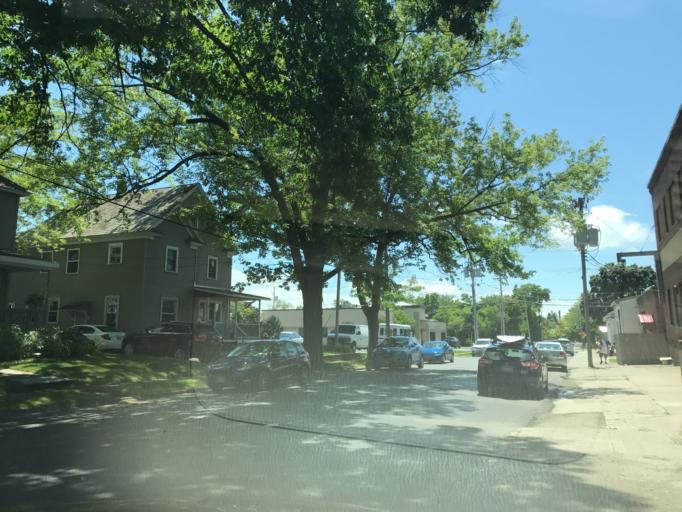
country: US
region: New York
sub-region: Warren County
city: Glens Falls
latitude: 43.3183
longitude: -73.6399
